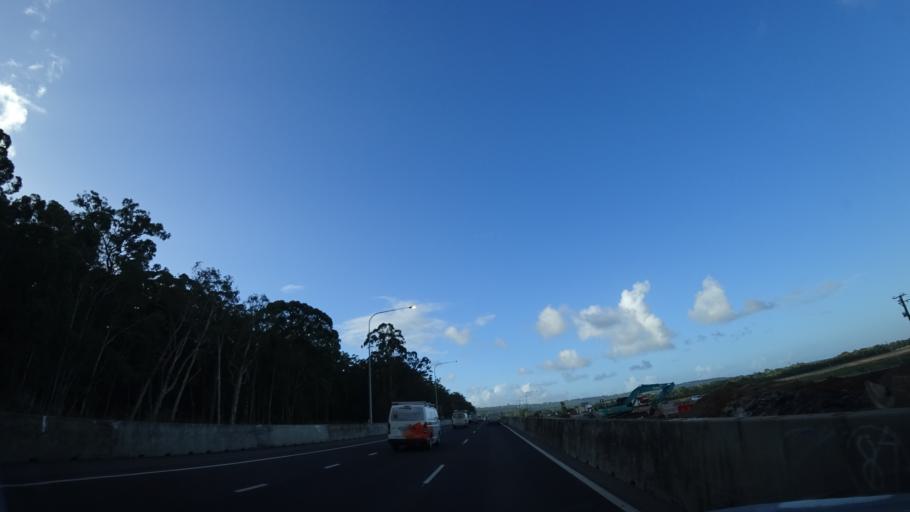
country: AU
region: Queensland
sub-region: Sunshine Coast
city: Buderim
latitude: -26.7397
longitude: 153.0470
